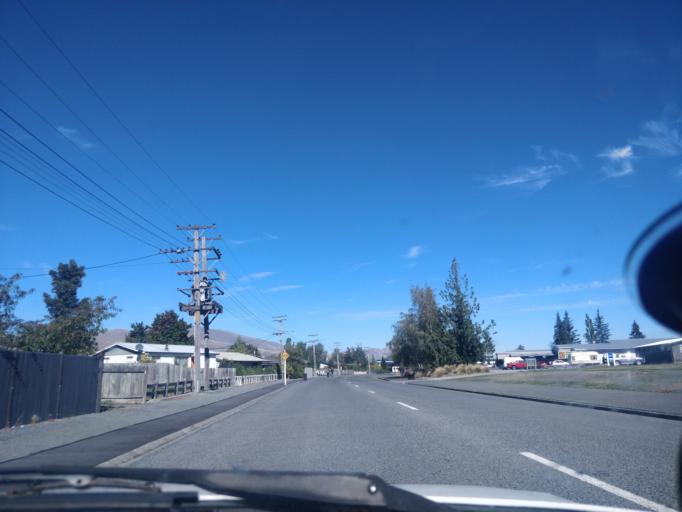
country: NZ
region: Canterbury
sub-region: Timaru District
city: Pleasant Point
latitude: -44.2555
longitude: 170.1013
